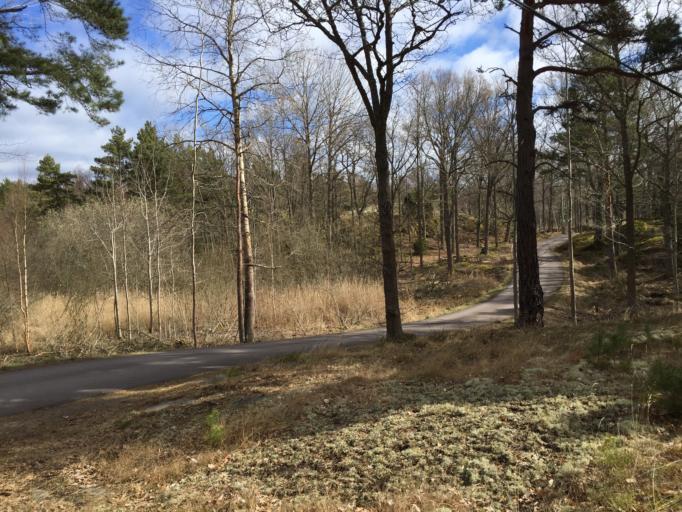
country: SE
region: Kalmar
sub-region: Oskarshamns Kommun
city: Oskarshamn
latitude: 57.2319
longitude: 16.4900
